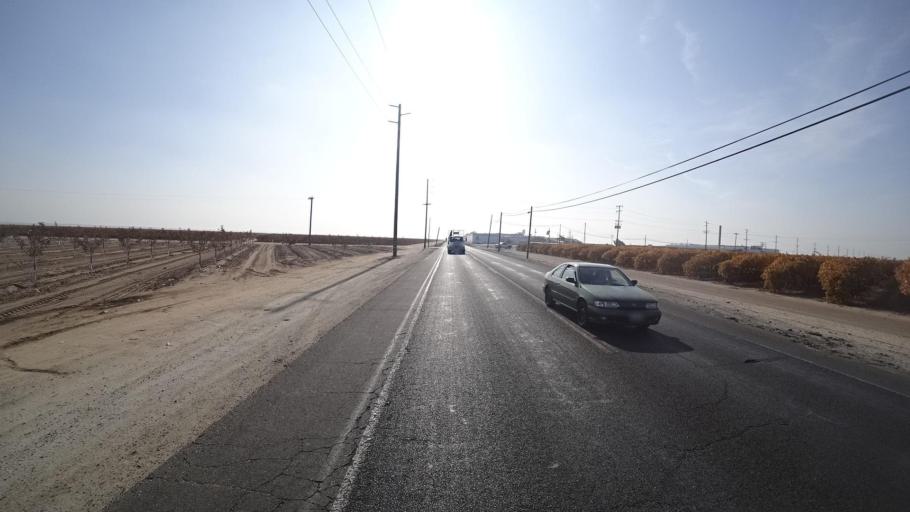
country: US
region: California
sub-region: Tulare County
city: Richgrove
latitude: 35.7770
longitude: -119.1231
